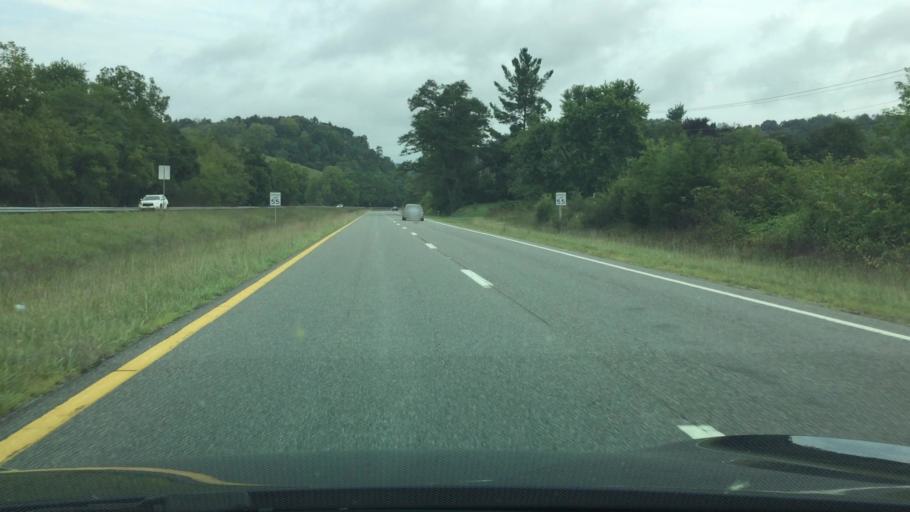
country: US
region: Virginia
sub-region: City of Radford
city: Radford
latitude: 37.1036
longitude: -80.5182
